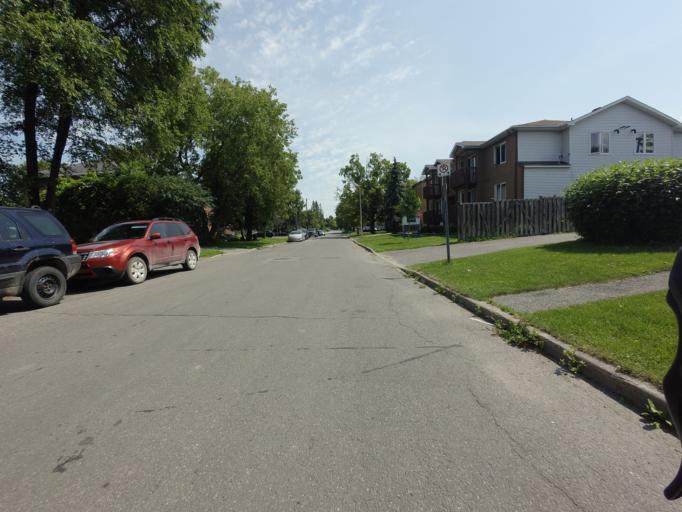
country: CA
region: Ontario
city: Ottawa
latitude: 45.3791
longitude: -75.7286
